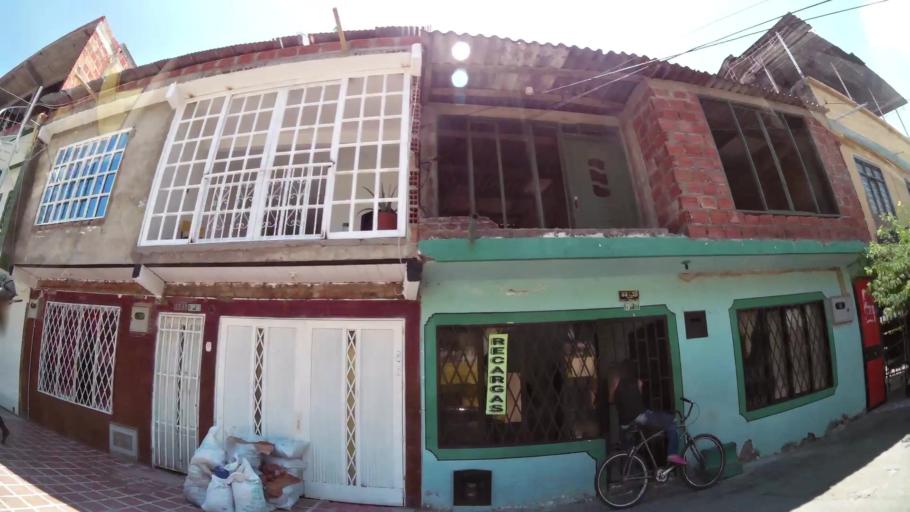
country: CO
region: Valle del Cauca
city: Cali
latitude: 3.4300
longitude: -76.5050
